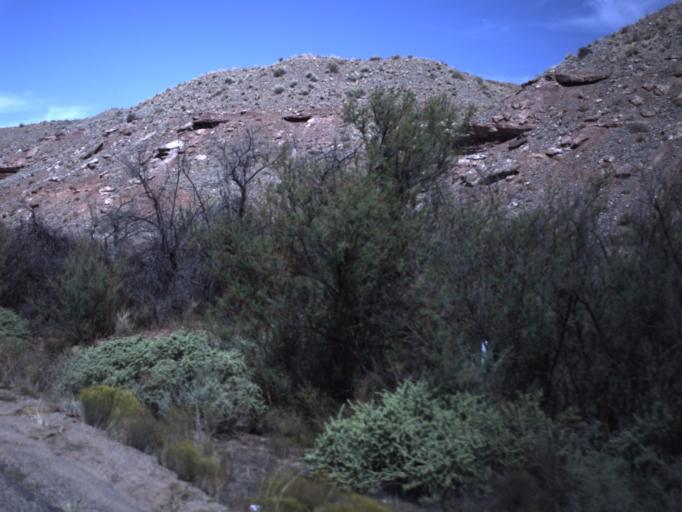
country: US
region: Colorado
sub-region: Montezuma County
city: Towaoc
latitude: 37.2223
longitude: -109.2020
